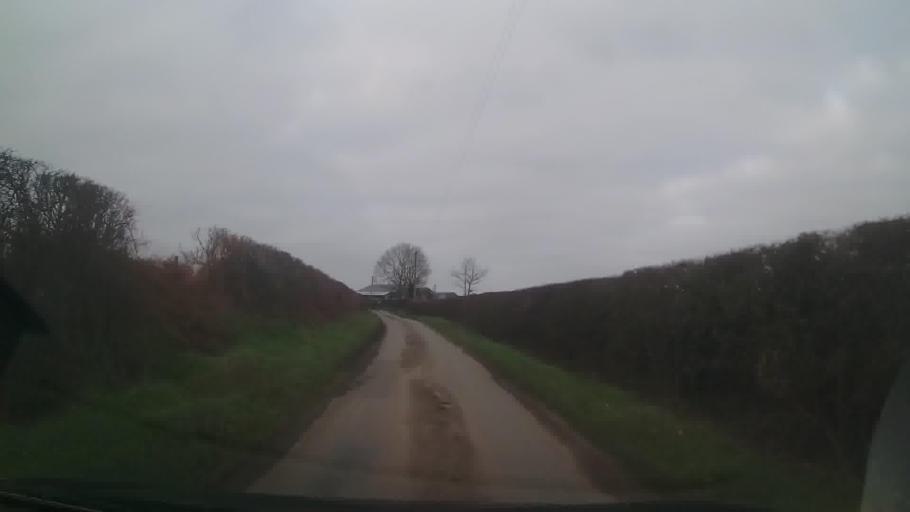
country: GB
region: England
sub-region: Shropshire
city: Petton
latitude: 52.7970
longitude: -2.8174
